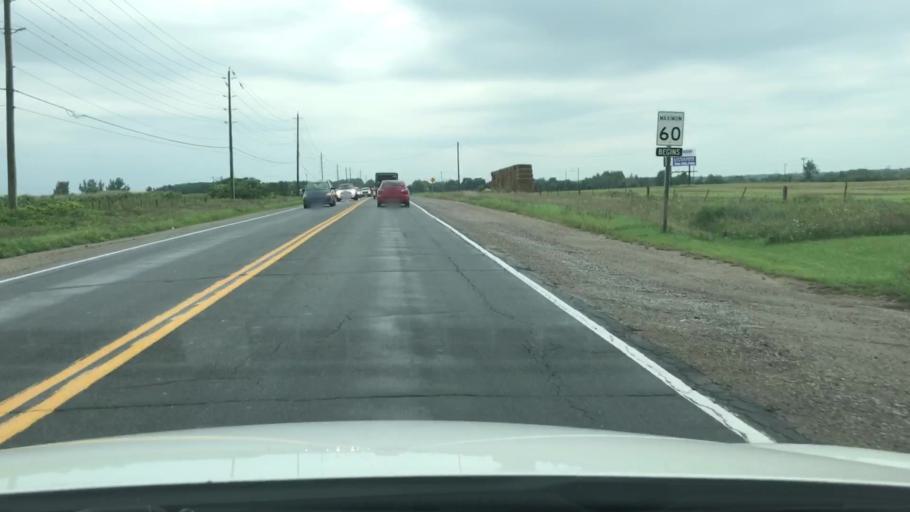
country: CA
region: Ontario
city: Innisfil
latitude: 44.3332
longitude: -79.6217
